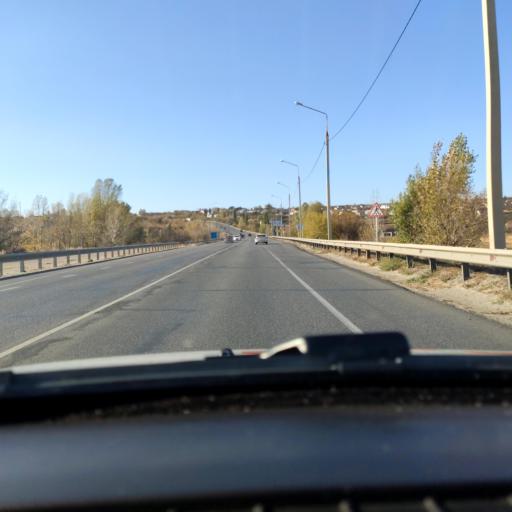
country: RU
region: Voronezj
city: Pridonskoy
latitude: 51.7248
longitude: 39.0582
